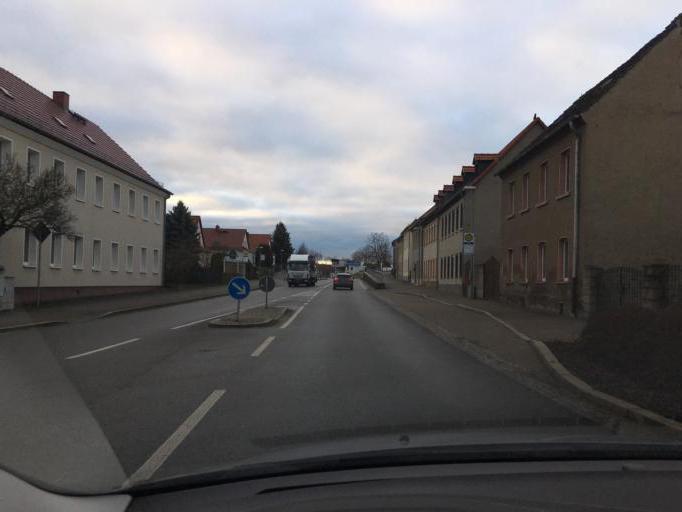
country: DE
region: Saxony
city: Frohburg
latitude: 51.0532
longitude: 12.5552
